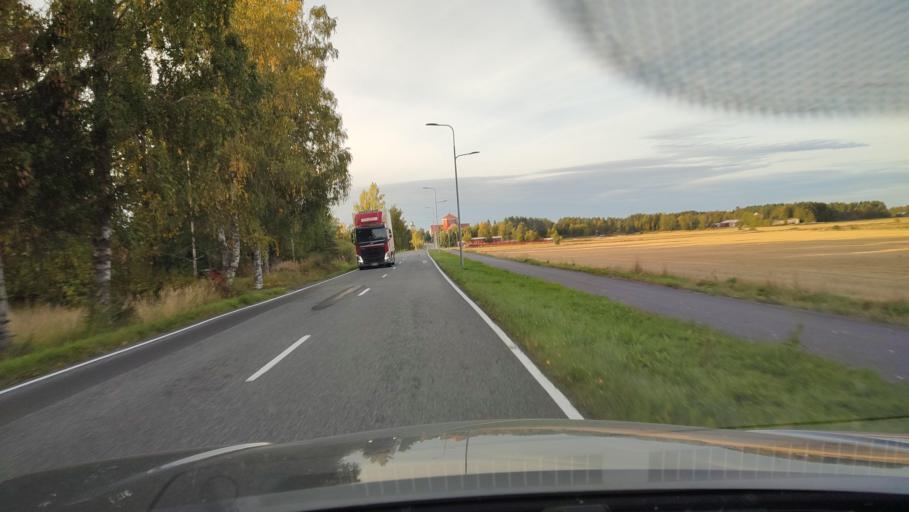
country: FI
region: Ostrobothnia
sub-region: Sydosterbotten
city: Kristinestad
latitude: 62.2393
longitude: 21.5209
